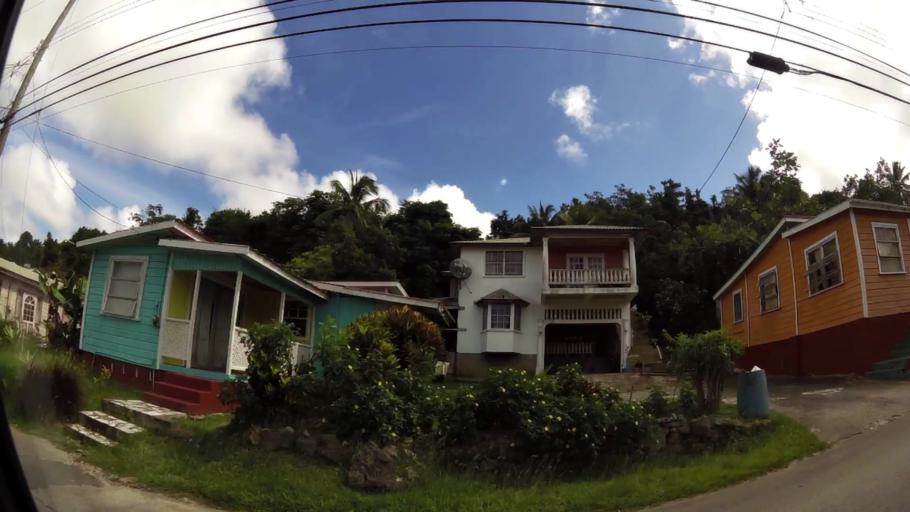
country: BB
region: Saint James
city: Holetown
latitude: 13.2103
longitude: -59.6058
